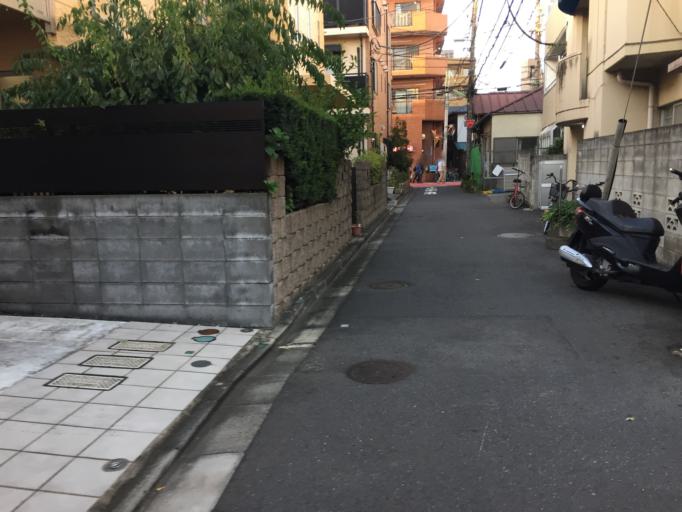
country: JP
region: Tokyo
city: Tokyo
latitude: 35.6425
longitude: 139.6671
